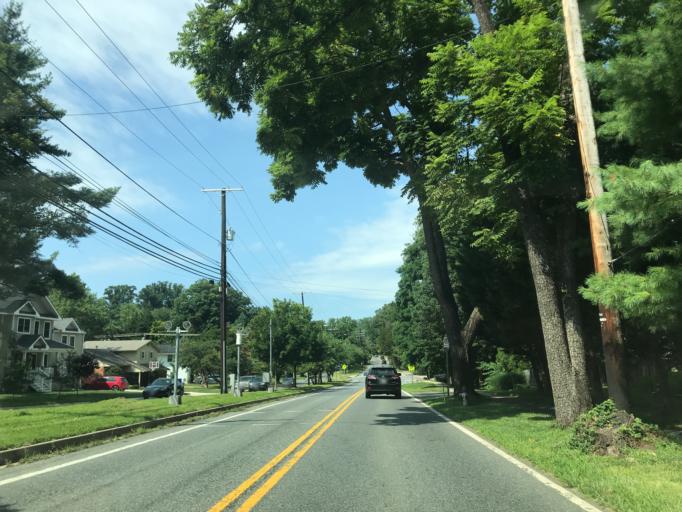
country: US
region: Maryland
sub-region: Montgomery County
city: Cabin John
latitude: 38.9874
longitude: -77.1307
